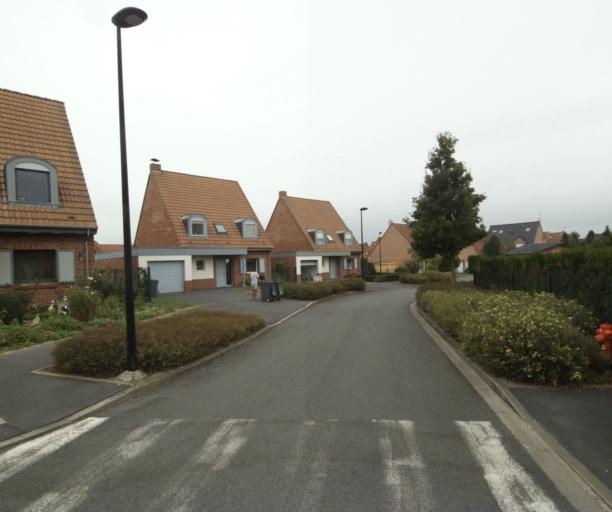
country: FR
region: Nord-Pas-de-Calais
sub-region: Departement du Nord
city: Baisieux
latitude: 50.6105
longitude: 3.2496
